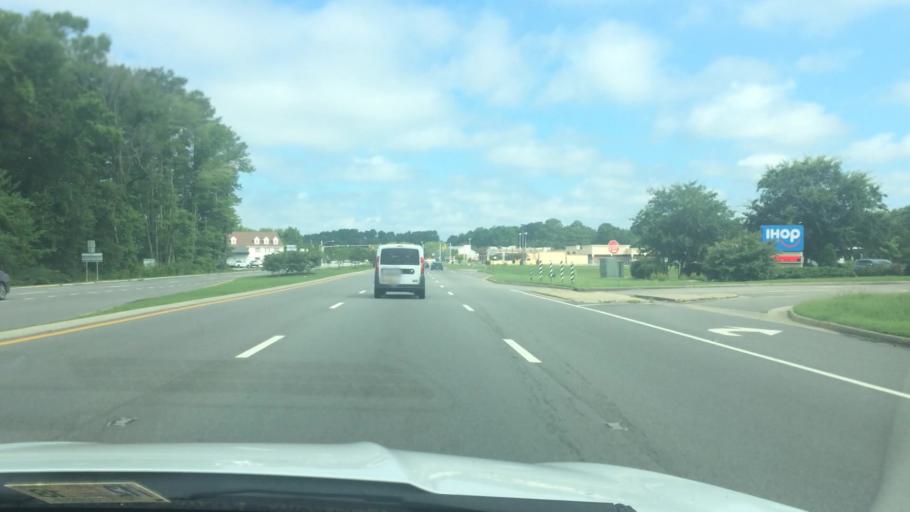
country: US
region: Virginia
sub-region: York County
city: Yorktown
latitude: 37.1612
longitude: -76.4638
